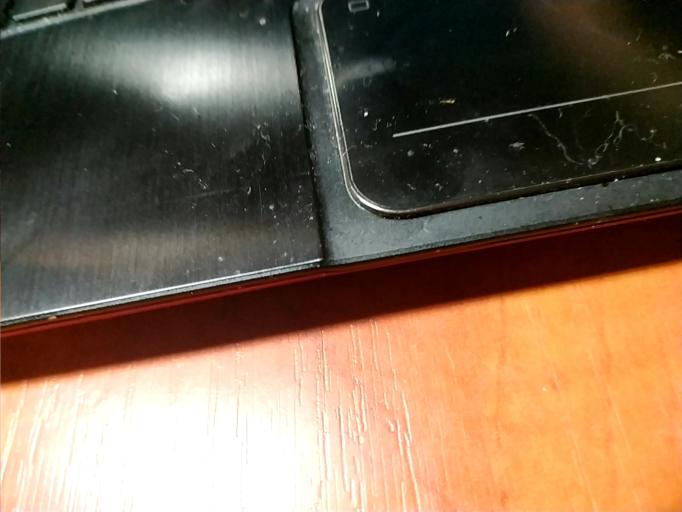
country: RU
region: Republic of Karelia
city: Kem'
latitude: 64.6082
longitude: 34.2039
